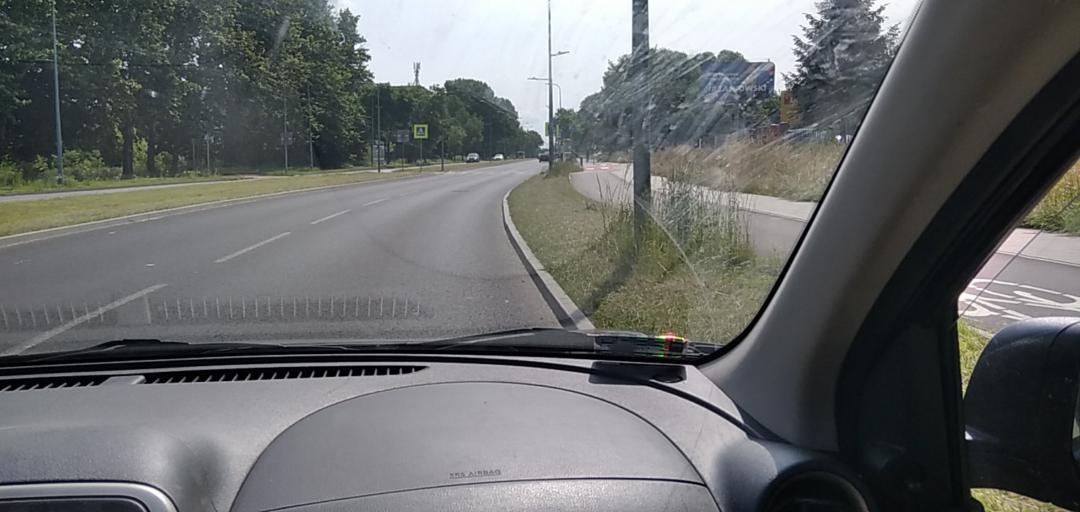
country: PL
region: Silesian Voivodeship
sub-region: Dabrowa Gornicza
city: Dabrowa Gornicza
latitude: 50.3423
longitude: 19.2347
